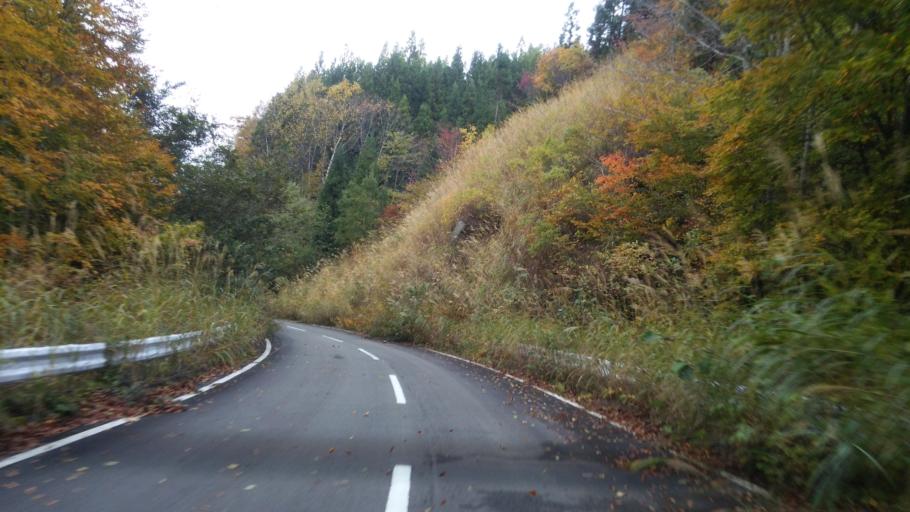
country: JP
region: Fukushima
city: Kitakata
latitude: 37.3799
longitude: 139.7298
